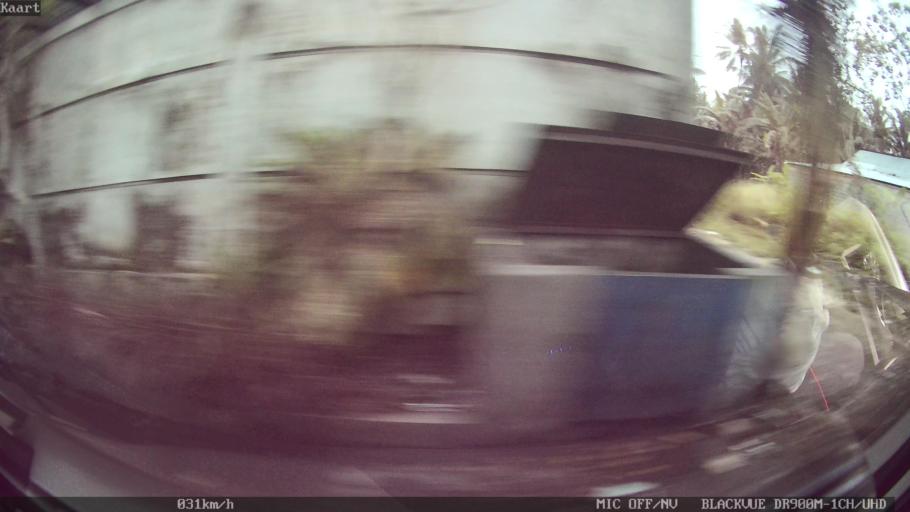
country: ID
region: Bali
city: Banjar Mambalkajanan
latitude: -8.5595
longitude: 115.2160
